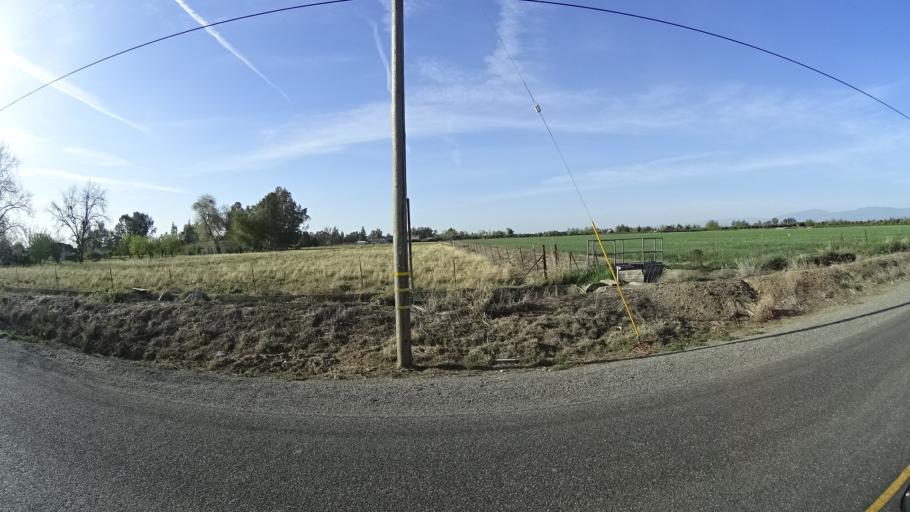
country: US
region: California
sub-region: Glenn County
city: Orland
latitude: 39.7259
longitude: -122.2169
